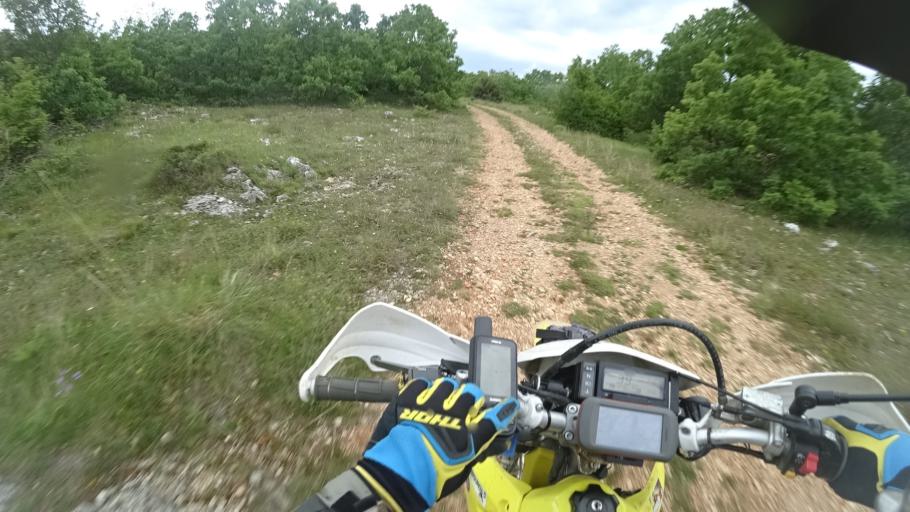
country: HR
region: Sibensko-Kniniska
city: Knin
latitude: 43.9853
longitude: 16.3307
